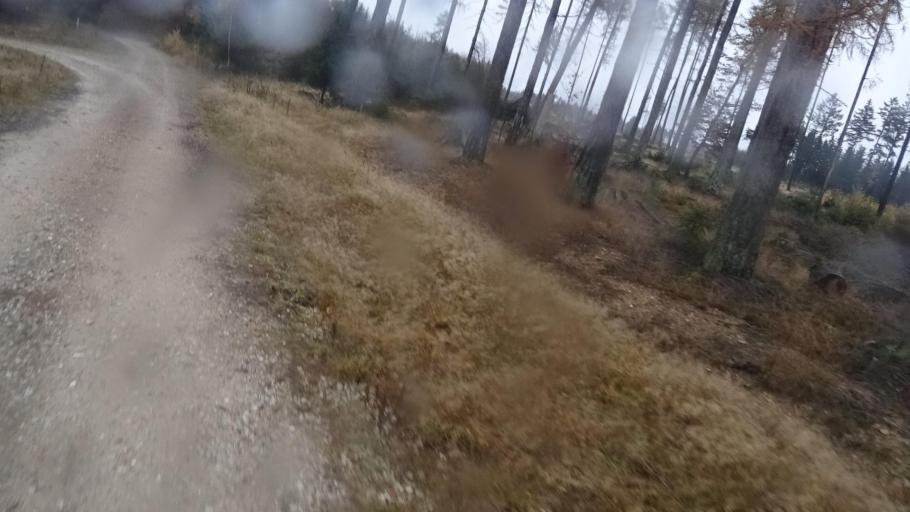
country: DE
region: Rheinland-Pfalz
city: Maisborn
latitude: 50.0957
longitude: 7.5937
